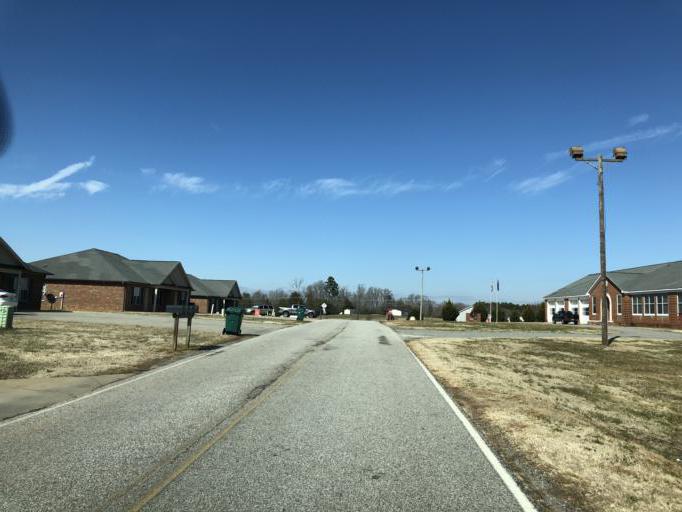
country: US
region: South Carolina
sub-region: Cherokee County
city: East Gaffney
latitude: 35.1373
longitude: -81.6672
